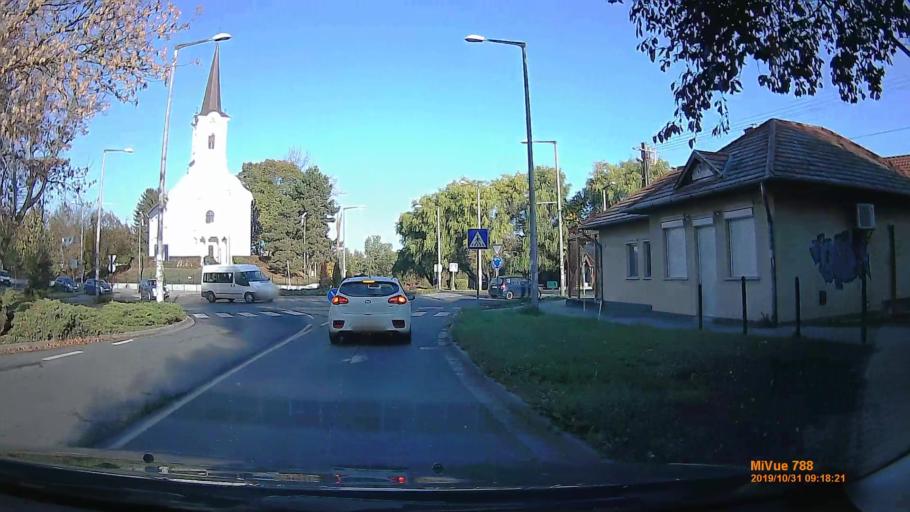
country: HU
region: Pest
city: Gyomro
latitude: 47.4129
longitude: 19.3975
